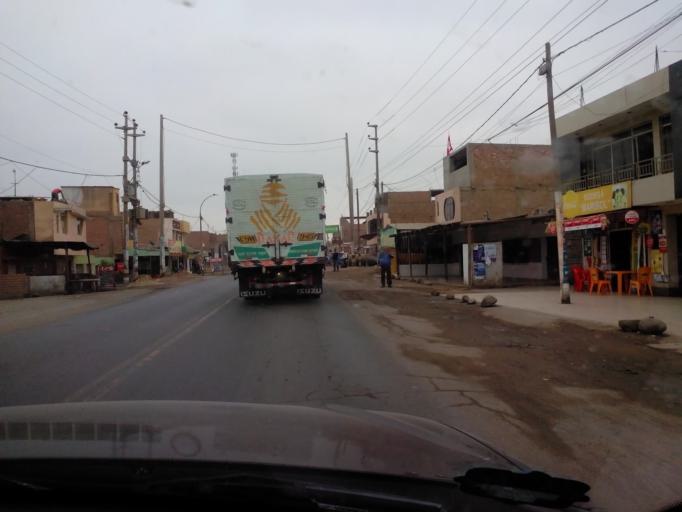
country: PE
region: Ica
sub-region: Provincia de Chincha
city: Chincha Alta
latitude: -13.4303
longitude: -76.1341
